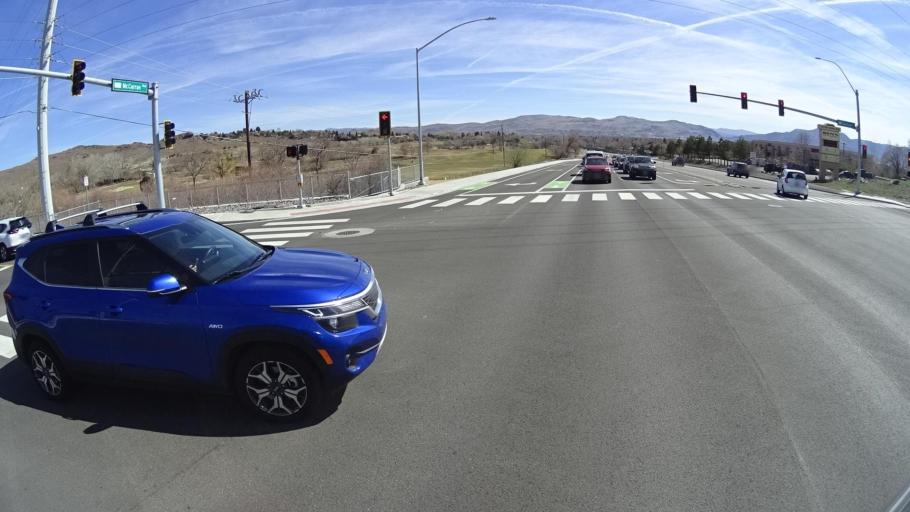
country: US
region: Nevada
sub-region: Washoe County
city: Sparks
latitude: 39.5575
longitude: -119.7727
